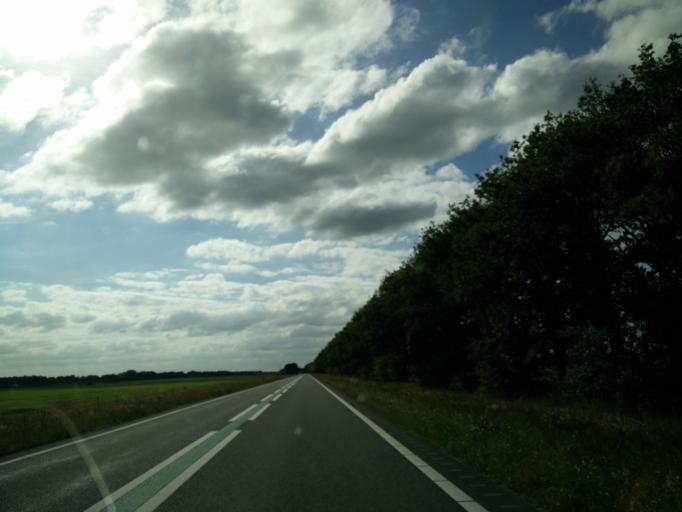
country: NL
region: Drenthe
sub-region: Gemeente Coevorden
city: Dalen
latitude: 52.8232
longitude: 6.6380
